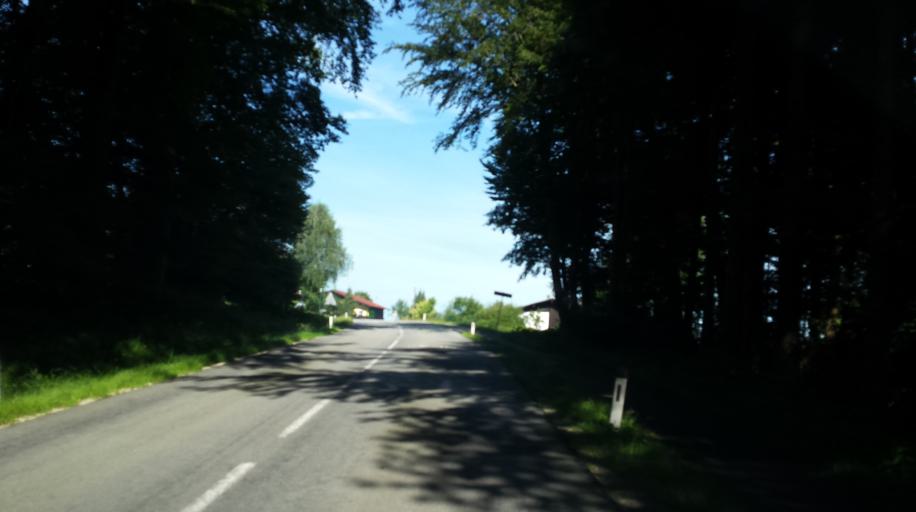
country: AT
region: Upper Austria
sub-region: Politischer Bezirk Vocklabruck
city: Sankt Georgen im Attergau
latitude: 47.9446
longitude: 13.4636
